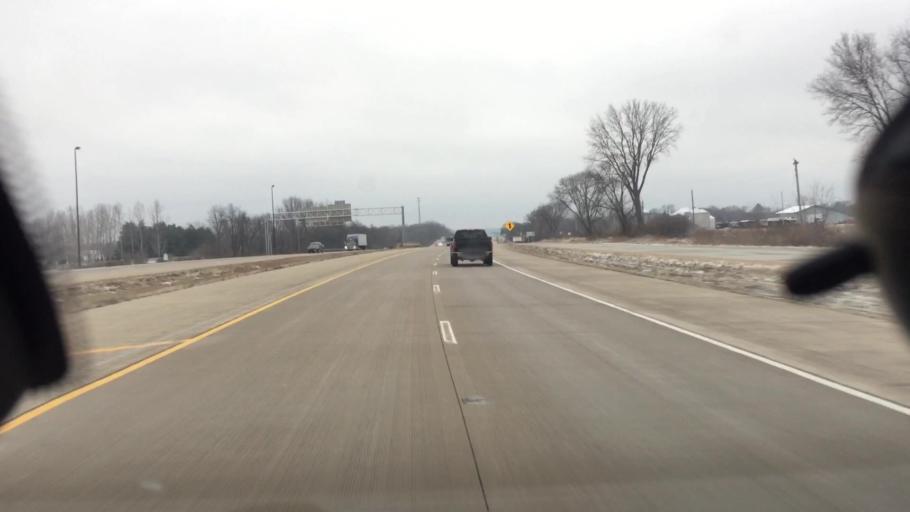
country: US
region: Iowa
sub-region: Scott County
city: Le Claire
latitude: 41.5548
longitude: -90.3418
